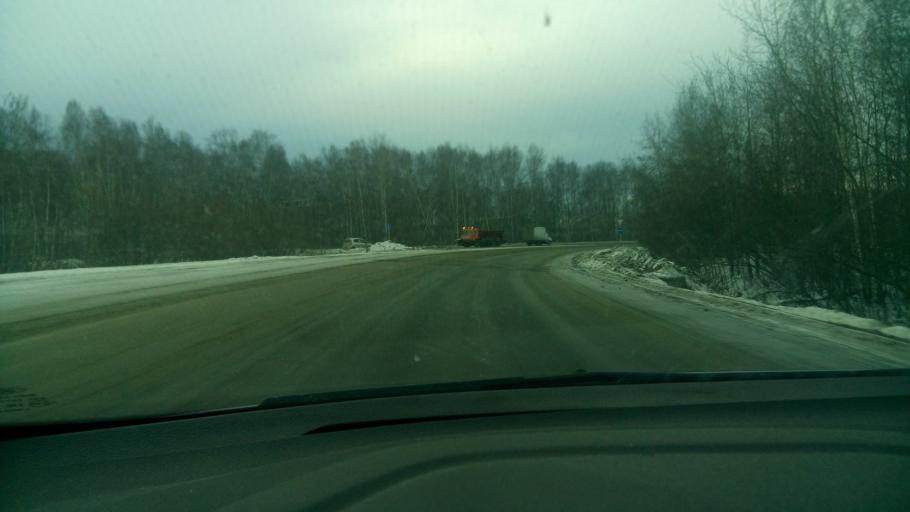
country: RU
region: Sverdlovsk
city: Istok
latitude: 56.7592
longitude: 60.7647
